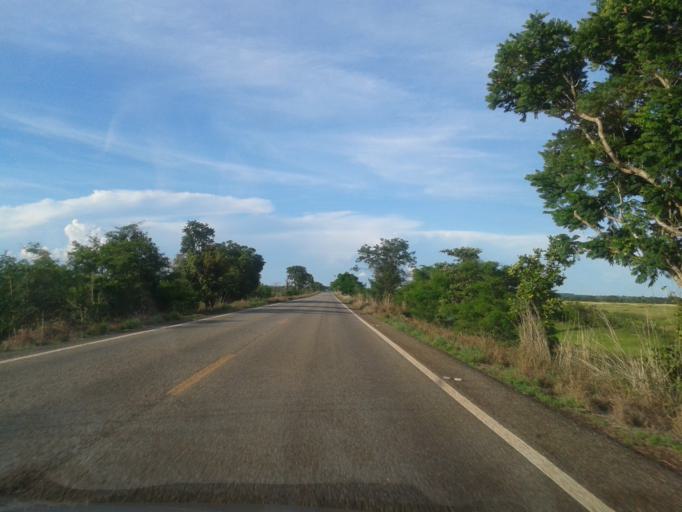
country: BR
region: Goias
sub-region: Sao Miguel Do Araguaia
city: Sao Miguel do Araguaia
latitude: -13.5809
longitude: -50.3153
